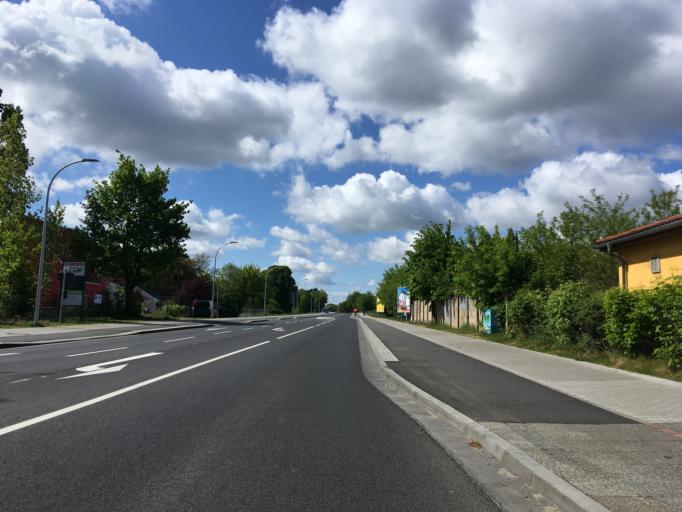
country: DE
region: Brandenburg
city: Oranienburg
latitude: 52.7445
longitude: 13.2551
